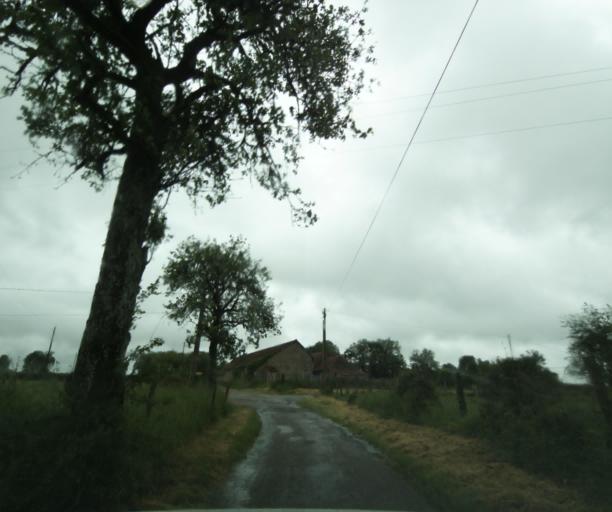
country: FR
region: Bourgogne
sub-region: Departement de Saone-et-Loire
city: Charolles
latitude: 46.4847
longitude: 4.4151
